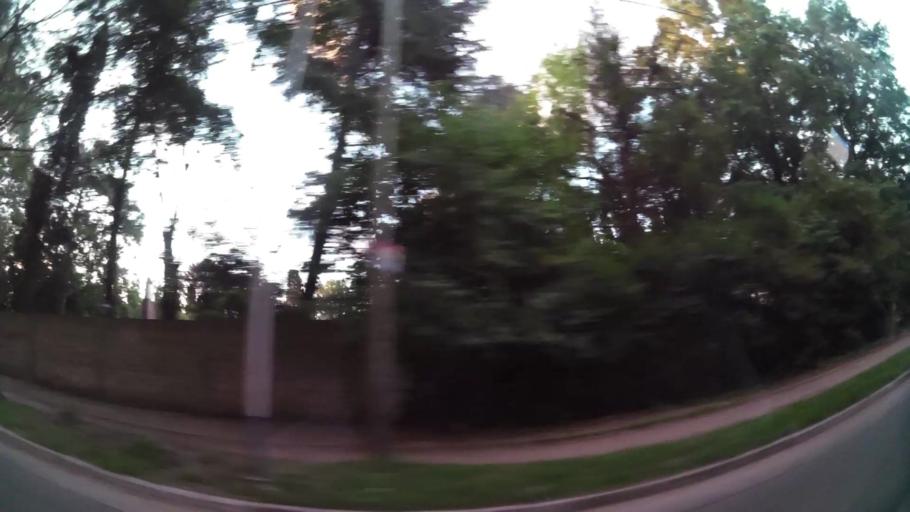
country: AR
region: Buenos Aires
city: Santa Catalina - Dique Lujan
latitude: -34.4808
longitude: -58.7743
